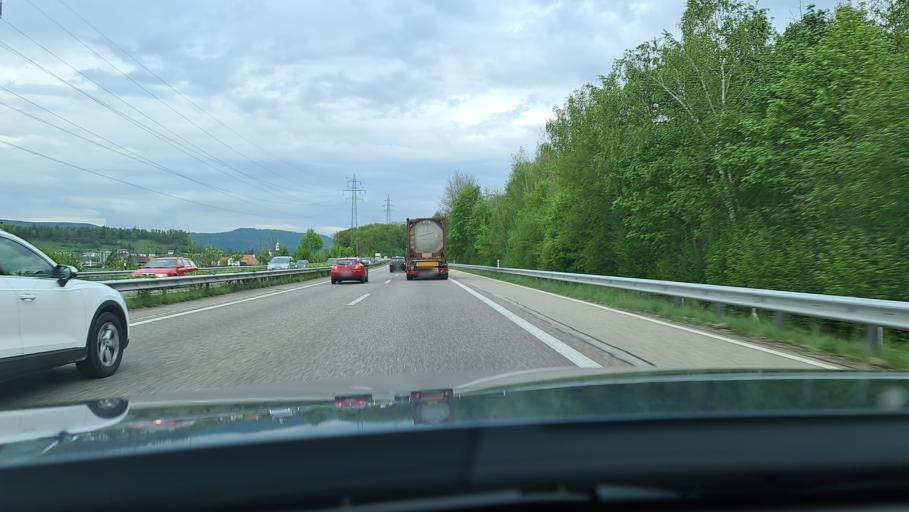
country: CH
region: Aargau
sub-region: Bezirk Aarau
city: Oberentfelden
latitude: 47.3572
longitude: 8.0643
